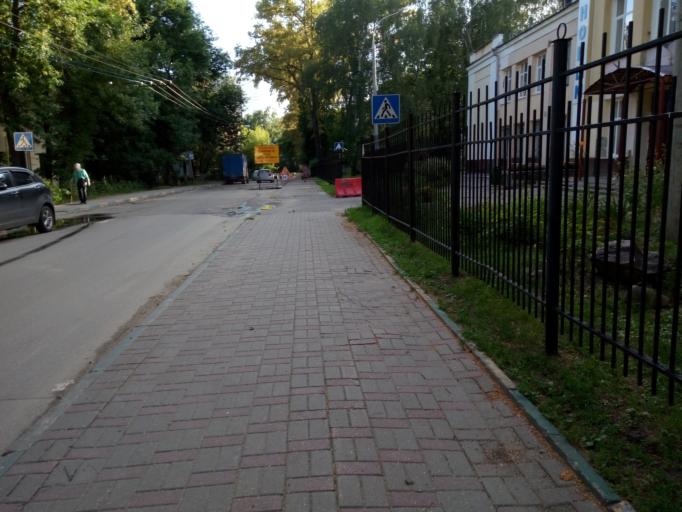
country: RU
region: Nizjnij Novgorod
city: Nizhniy Novgorod
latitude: 56.2695
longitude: 43.9802
